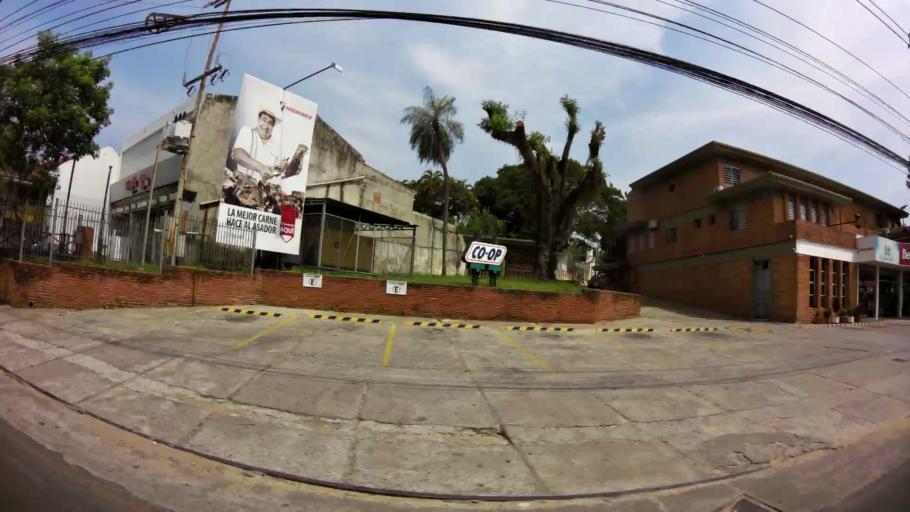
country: PY
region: Asuncion
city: Asuncion
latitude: -25.2875
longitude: -57.5986
